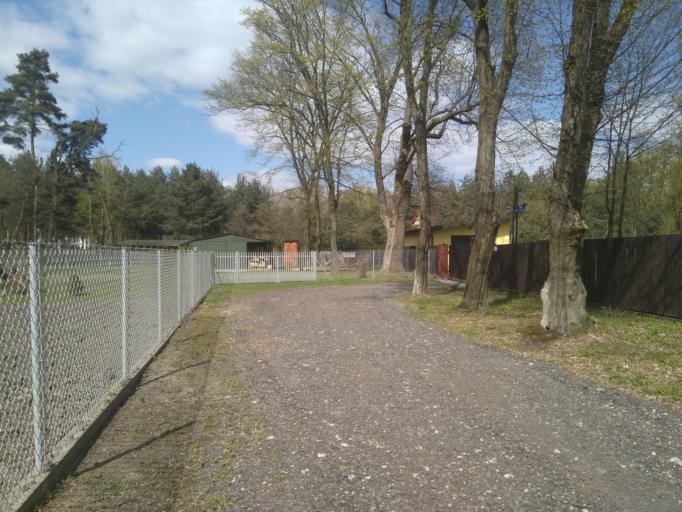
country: PL
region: Masovian Voivodeship
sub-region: Powiat zyrardowski
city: Radziejowice
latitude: 52.0689
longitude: 20.5737
